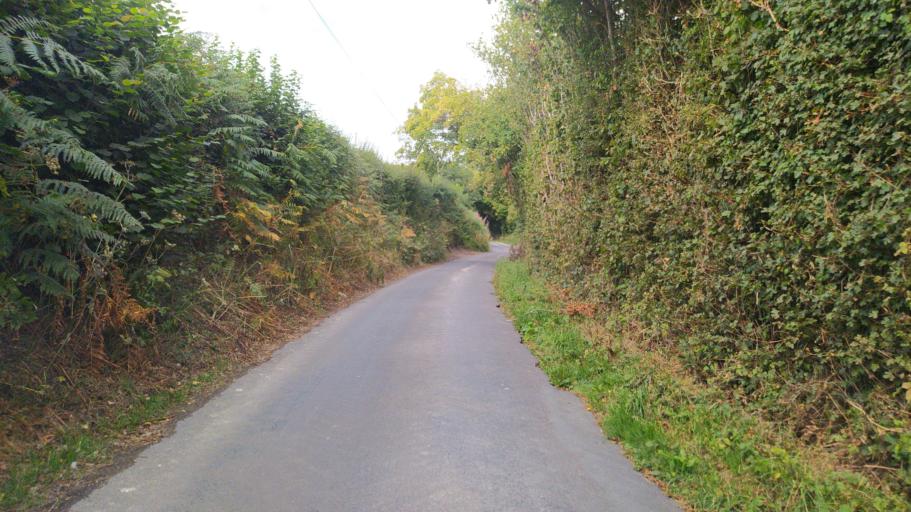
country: GB
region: England
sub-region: Hampshire
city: Petersfield
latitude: 50.9896
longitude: -0.9893
